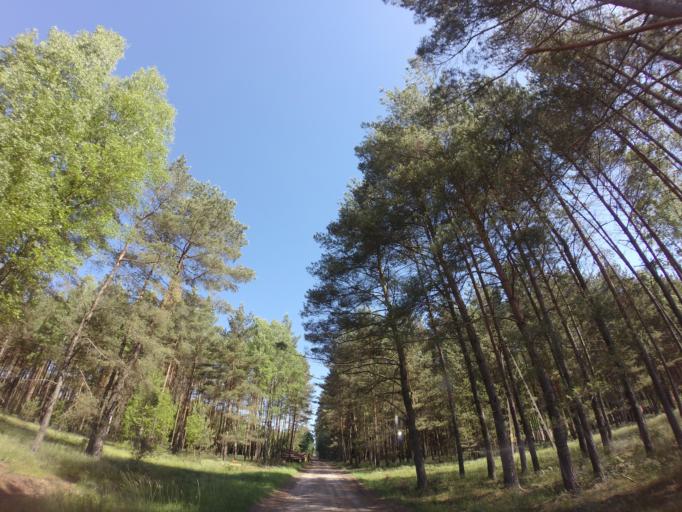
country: PL
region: West Pomeranian Voivodeship
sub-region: Powiat walecki
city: Czlopa
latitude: 53.1335
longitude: 15.9644
